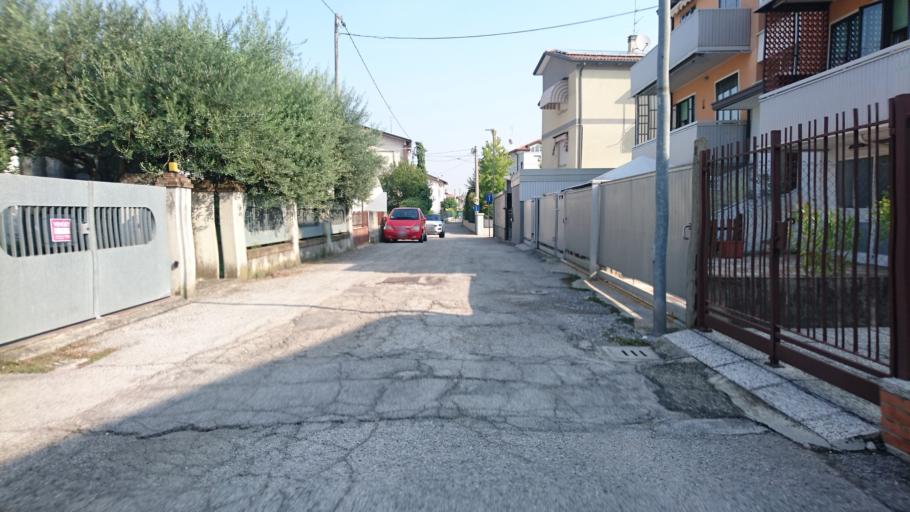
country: IT
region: Veneto
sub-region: Provincia di Padova
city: Albignasego
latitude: 45.3462
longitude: 11.8651
